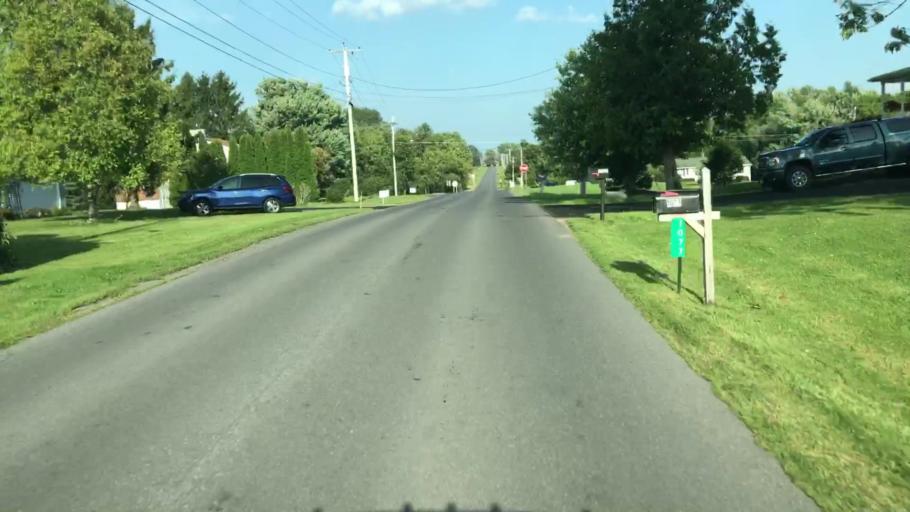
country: US
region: New York
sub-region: Onondaga County
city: Skaneateles
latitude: 42.9641
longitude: -76.4278
